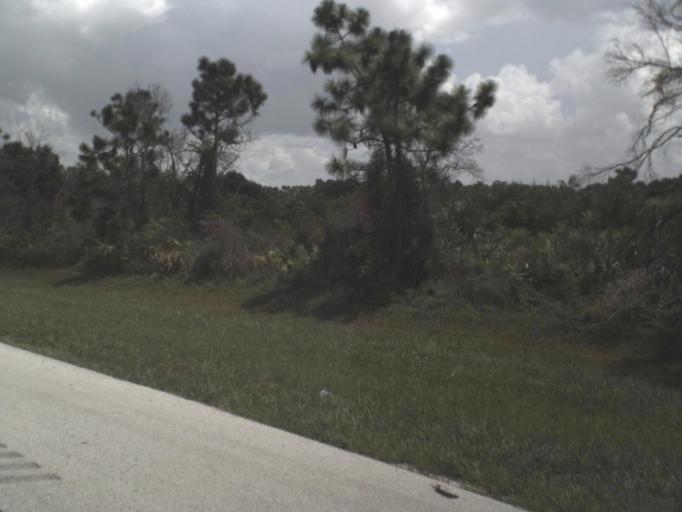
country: US
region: Florida
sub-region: Hillsborough County
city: Ruskin
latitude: 27.7016
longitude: -82.3955
